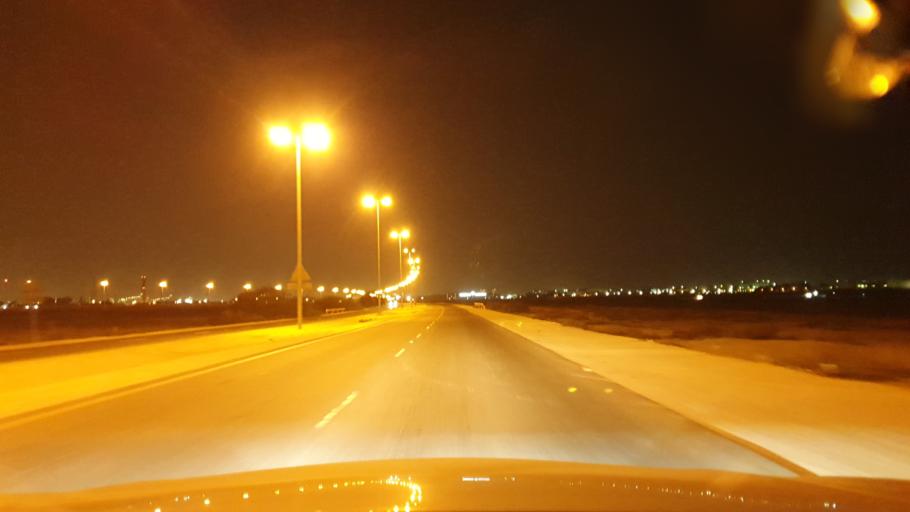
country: BH
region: Northern
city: Ar Rifa'
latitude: 26.0632
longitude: 50.6170
